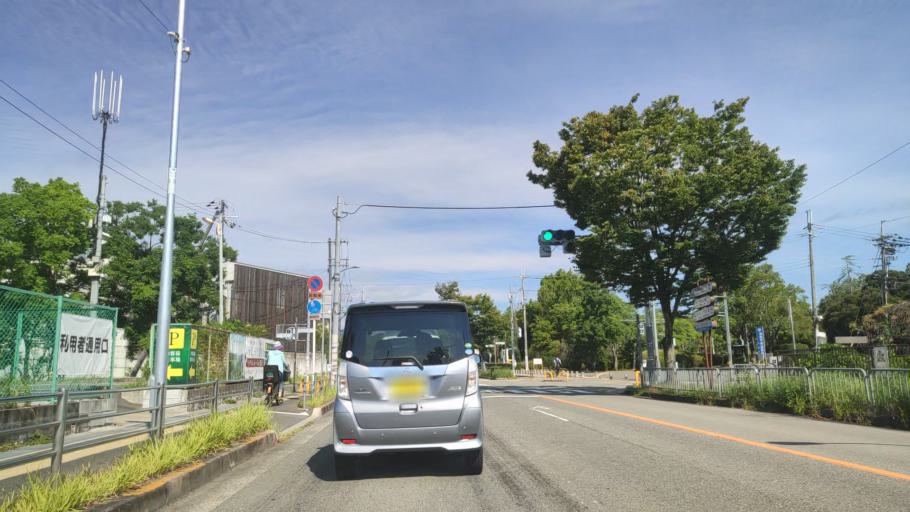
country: JP
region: Osaka
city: Mino
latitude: 34.8234
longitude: 135.5096
